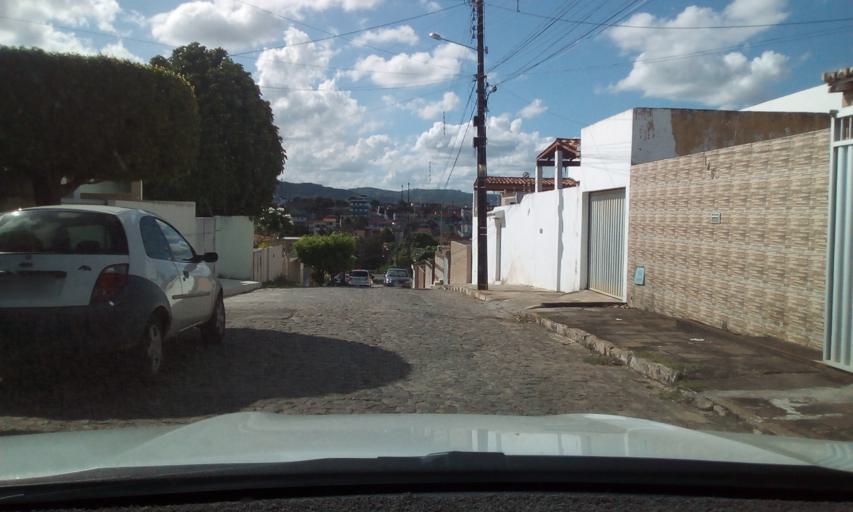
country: BR
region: Paraiba
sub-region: Guarabira
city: Guarabira
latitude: -6.8677
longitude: -35.4871
